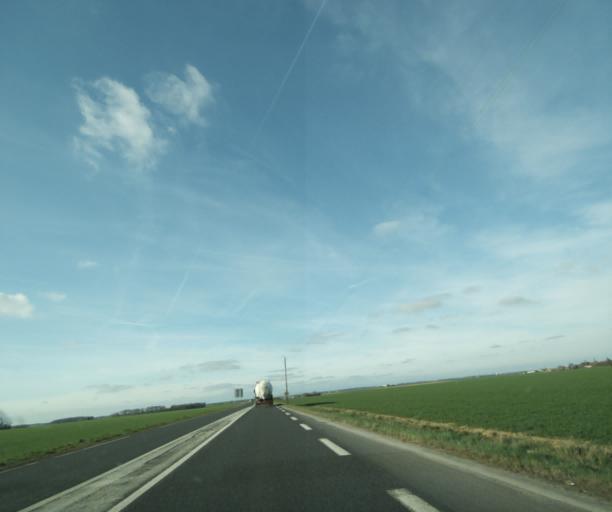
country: FR
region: Ile-de-France
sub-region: Departement des Yvelines
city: Ablis
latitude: 48.4856
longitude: 1.8479
